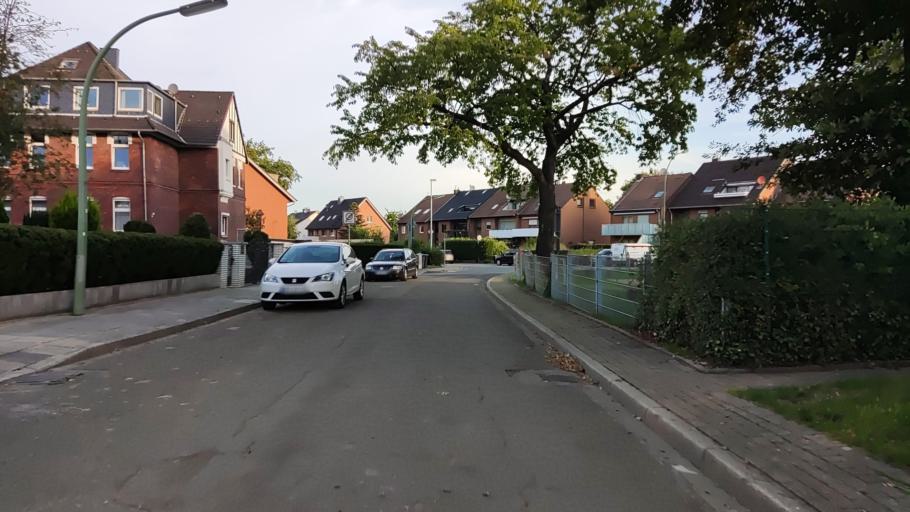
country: DE
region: North Rhine-Westphalia
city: Castrop-Rauxel
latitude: 51.5413
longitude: 7.2868
